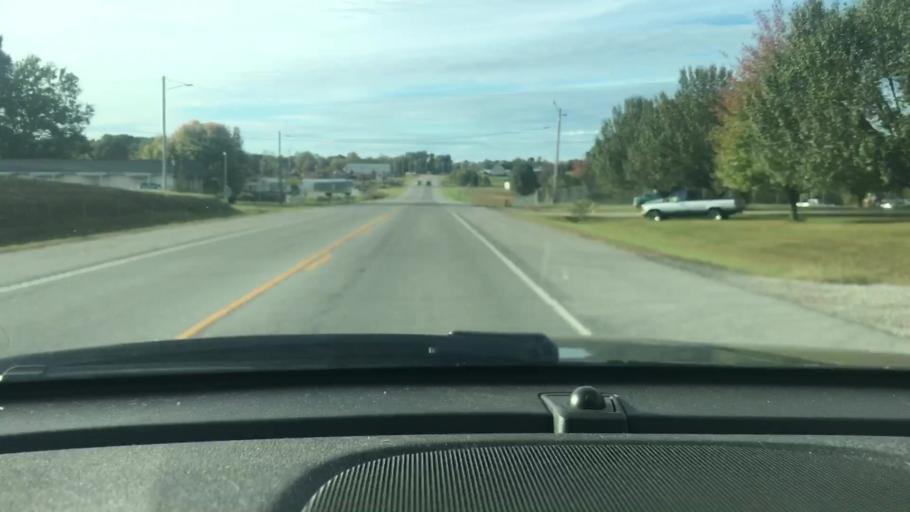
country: US
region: Tennessee
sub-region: Dickson County
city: White Bluff
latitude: 36.1301
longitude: -87.2312
